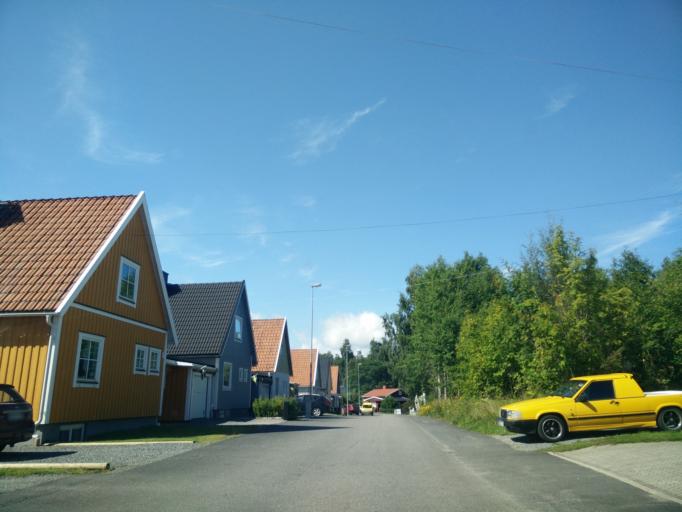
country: SE
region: Vaesternorrland
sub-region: Haernoesands Kommun
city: Haernoesand
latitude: 62.6345
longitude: 17.9146
